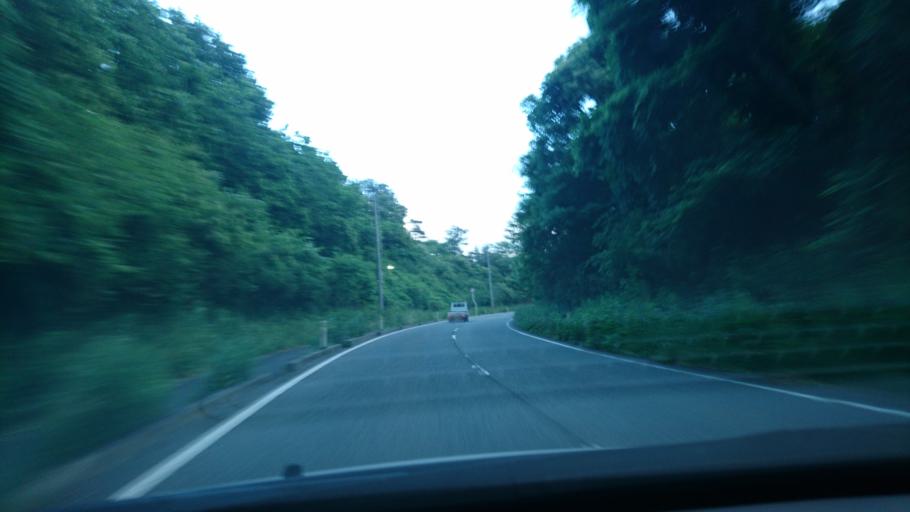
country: JP
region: Iwate
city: Ichinoseki
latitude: 38.7899
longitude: 141.0558
